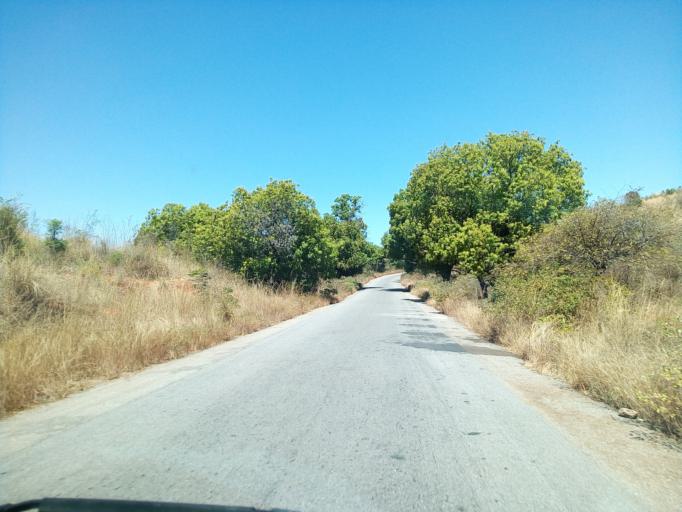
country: MG
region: Betsiboka
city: Maevatanana
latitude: -16.8084
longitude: 47.0045
